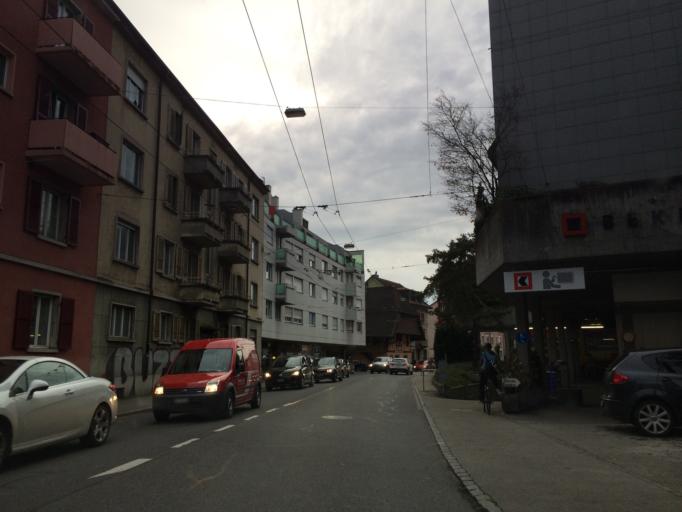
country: CH
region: Bern
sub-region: Biel/Bienne District
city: Brugg
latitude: 47.1468
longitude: 7.2730
